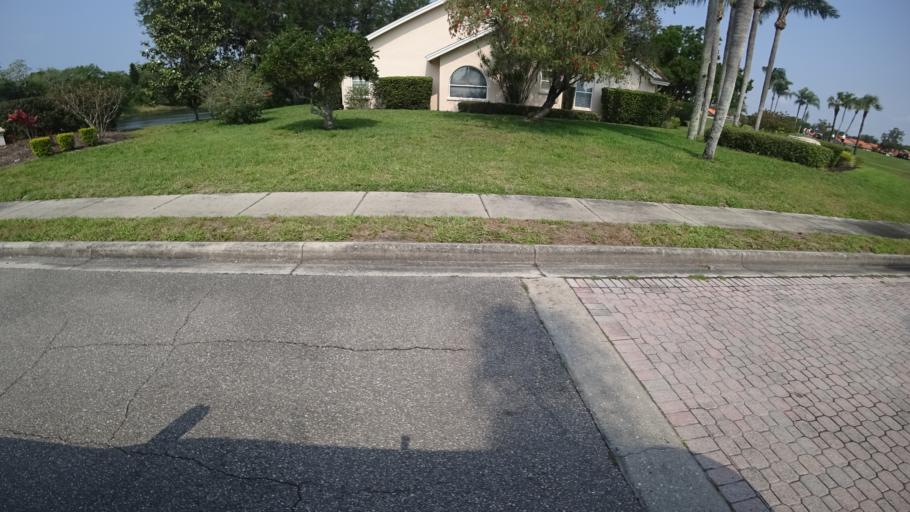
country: US
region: Florida
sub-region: Manatee County
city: Samoset
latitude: 27.4504
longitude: -82.5122
